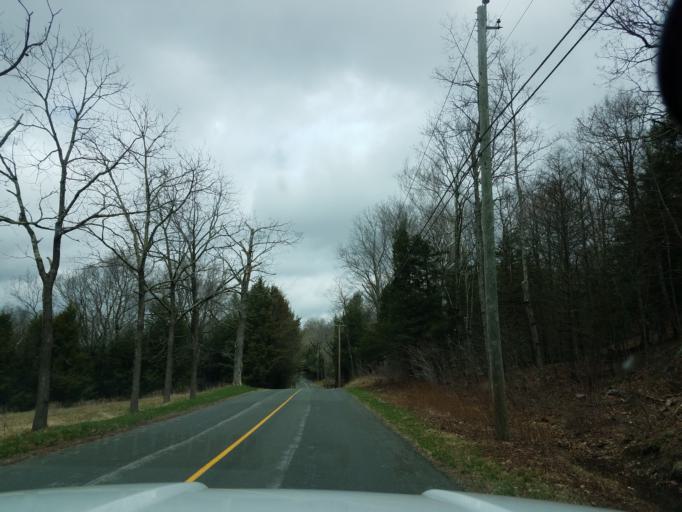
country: US
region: Connecticut
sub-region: Litchfield County
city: Litchfield
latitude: 41.7807
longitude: -73.1769
